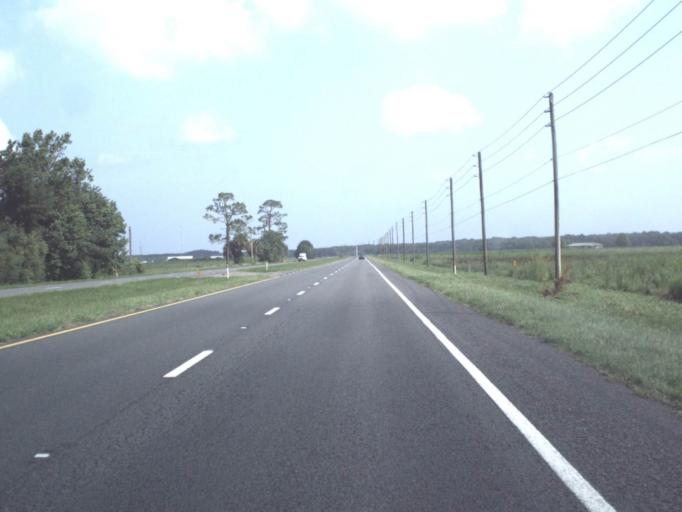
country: US
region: Florida
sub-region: Nassau County
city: Callahan
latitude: 30.6099
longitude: -81.8384
